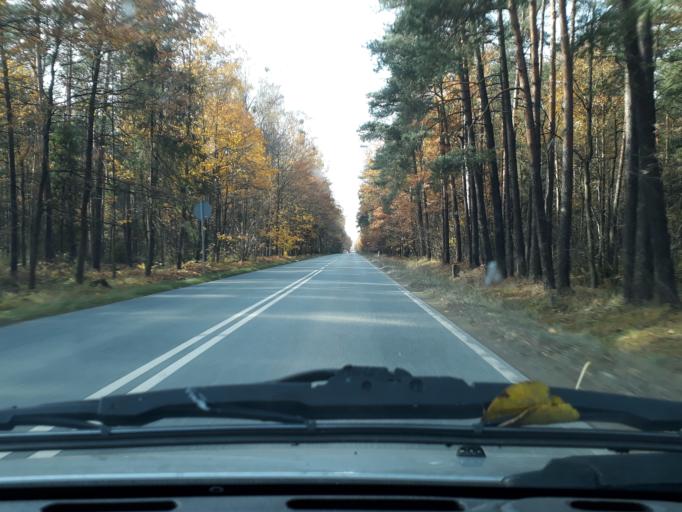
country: PL
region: Silesian Voivodeship
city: Wozniki
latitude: 50.5756
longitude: 19.0214
